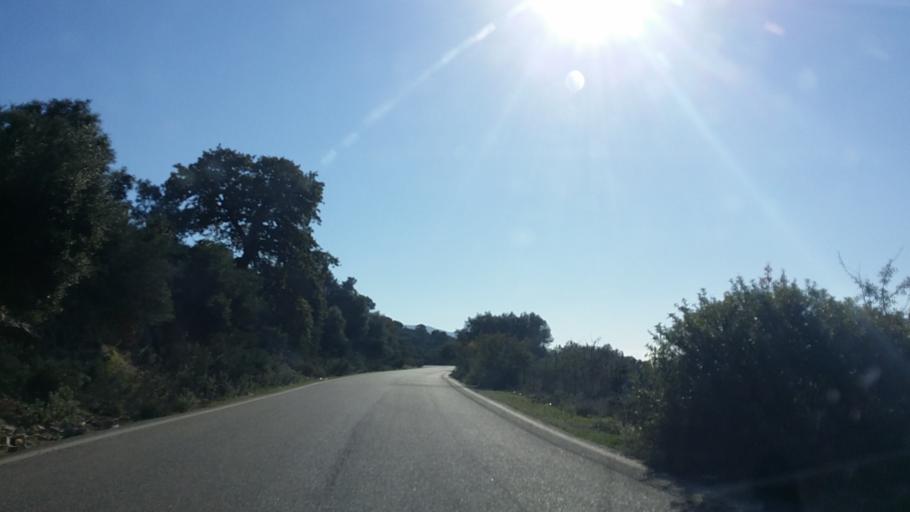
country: GR
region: West Greece
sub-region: Nomos Aitolias kai Akarnanias
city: Kandila
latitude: 38.7219
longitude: 20.8949
